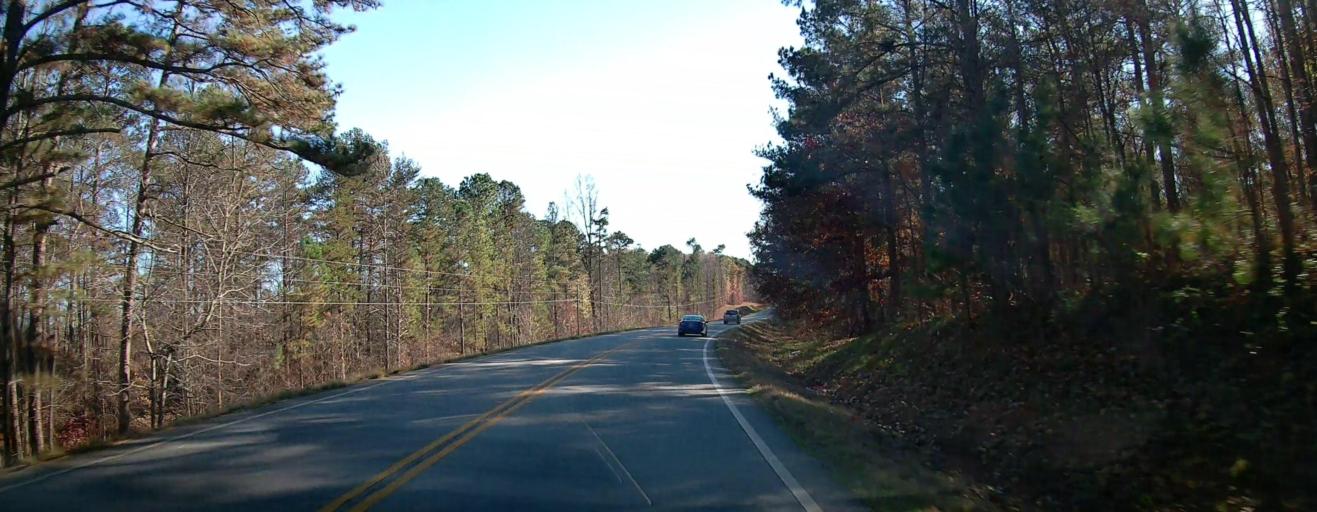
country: US
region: Georgia
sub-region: Hall County
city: Lula
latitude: 34.4396
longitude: -83.7180
